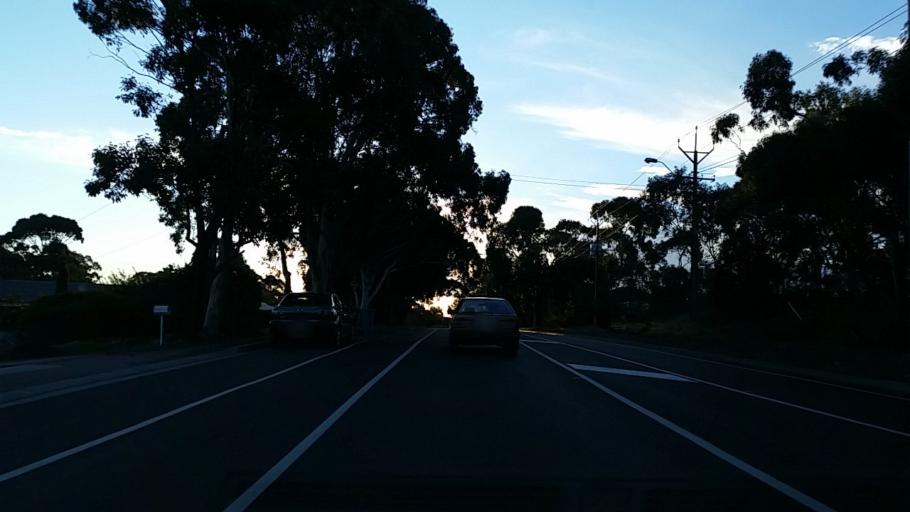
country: AU
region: South Australia
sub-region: Onkaparinga
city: Craigburn Farm
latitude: -35.0577
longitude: 138.6013
